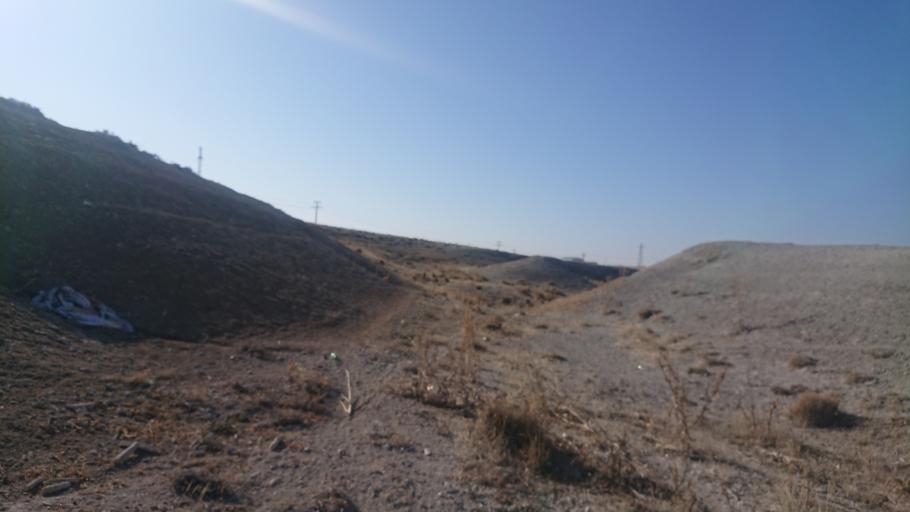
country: TR
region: Aksaray
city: Sultanhani
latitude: 38.2597
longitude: 33.5104
